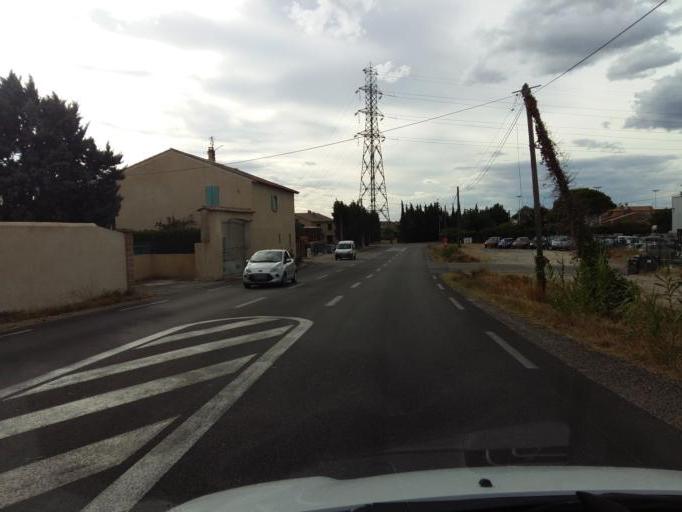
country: FR
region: Provence-Alpes-Cote d'Azur
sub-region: Departement du Vaucluse
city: Carpentras
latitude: 44.0319
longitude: 5.0463
